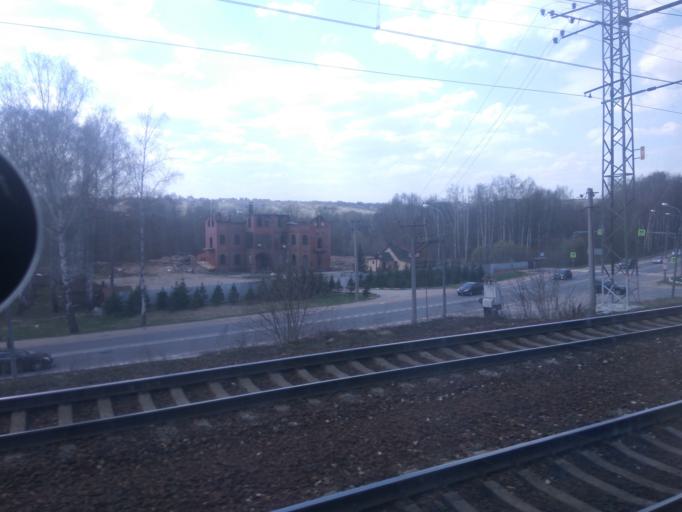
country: RU
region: Moskovskaya
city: Yakhroma
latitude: 56.3002
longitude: 37.4948
